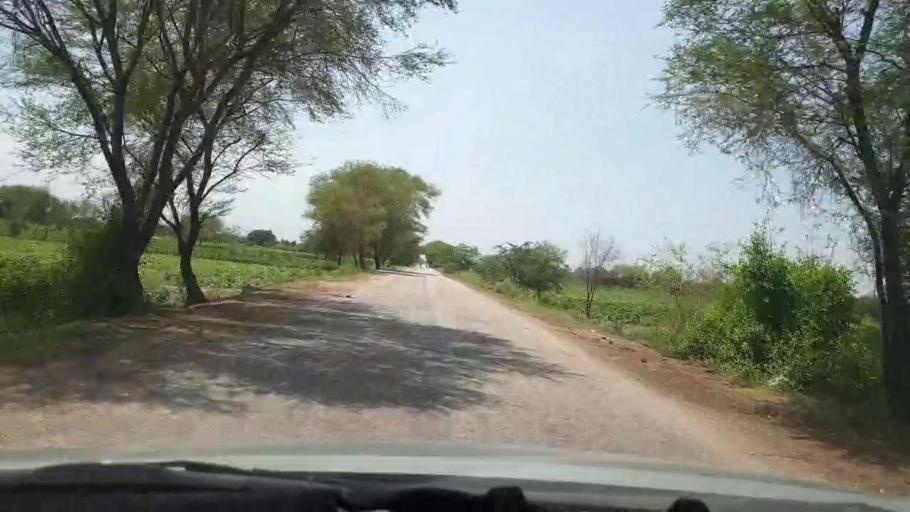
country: PK
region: Sindh
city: Pano Aqil
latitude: 27.6635
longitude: 69.1388
